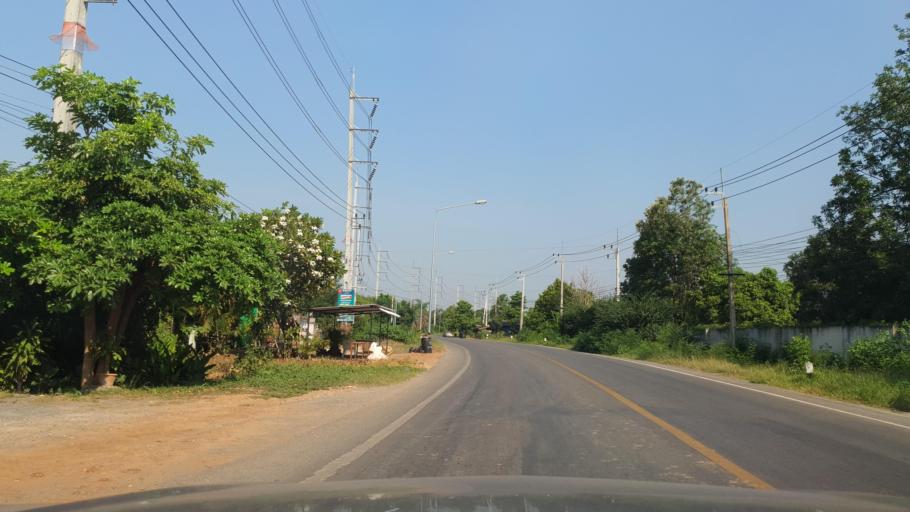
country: TH
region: Kanchanaburi
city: Kanchanaburi
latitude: 14.0381
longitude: 99.4773
